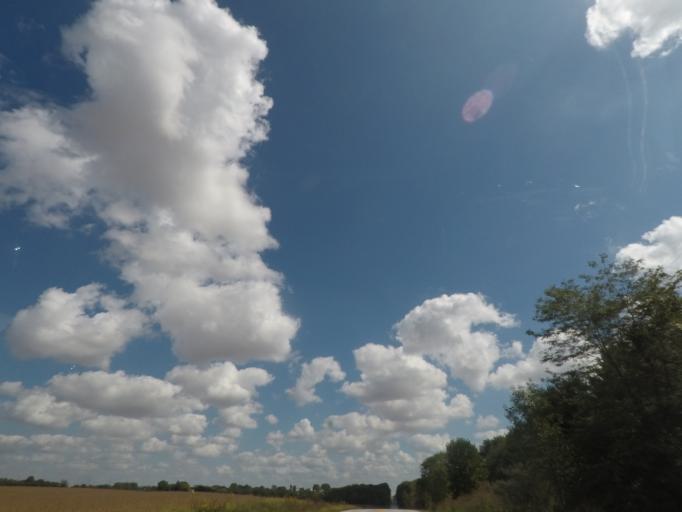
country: US
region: Iowa
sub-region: Story County
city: Nevada
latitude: 42.0777
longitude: -93.3634
